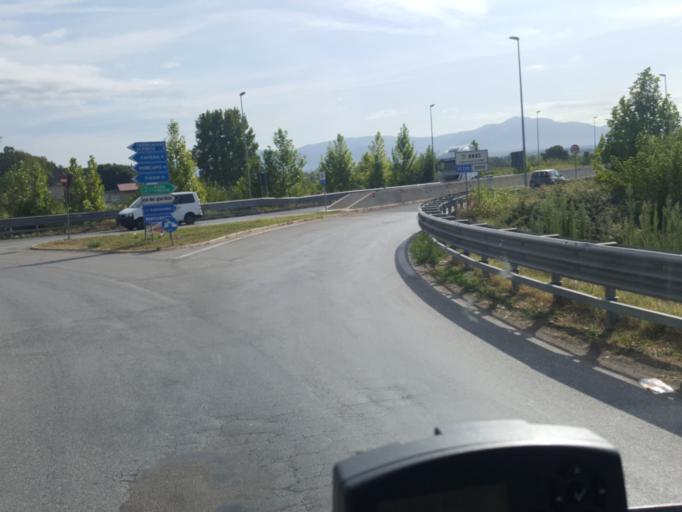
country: IT
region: Latium
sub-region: Citta metropolitana di Roma Capitale
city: Girardi-Bellavista-Terrazze
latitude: 42.0939
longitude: 12.5659
